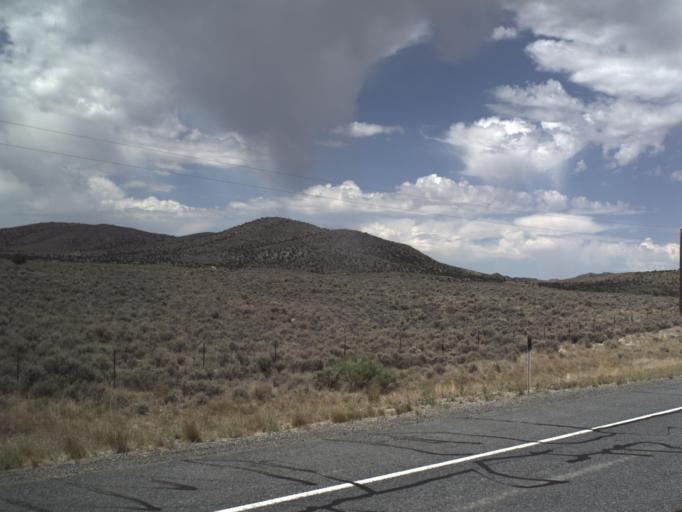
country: US
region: Utah
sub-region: Utah County
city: Eagle Mountain
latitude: 40.0752
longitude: -112.3407
